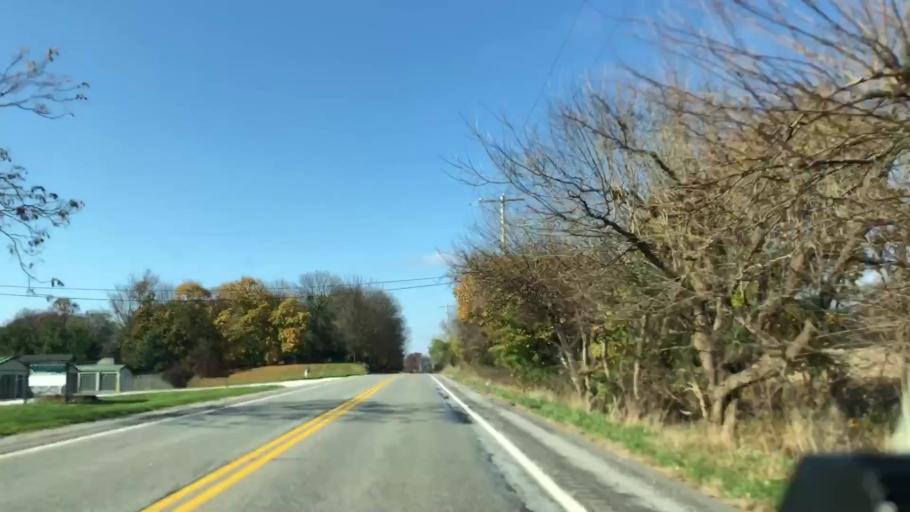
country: US
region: Pennsylvania
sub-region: Chester County
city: Kenilworth
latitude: 40.2181
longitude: -75.6080
